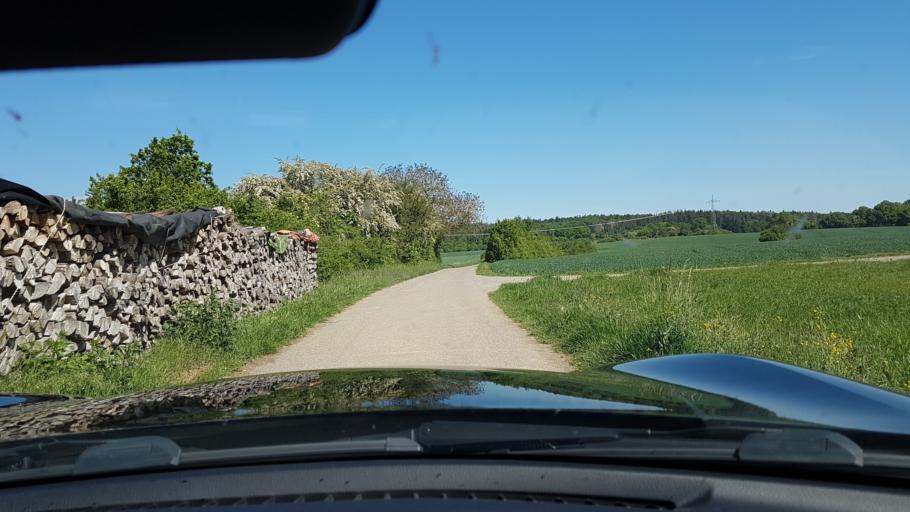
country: DE
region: Baden-Wuerttemberg
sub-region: Karlsruhe Region
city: Osterburken
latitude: 49.4367
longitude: 9.4215
